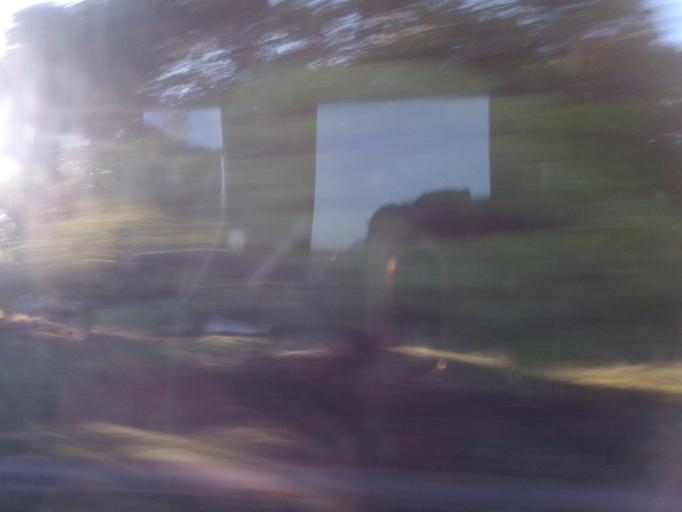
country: PA
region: Veraguas
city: Los Boquerones
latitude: 8.0813
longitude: -80.8952
